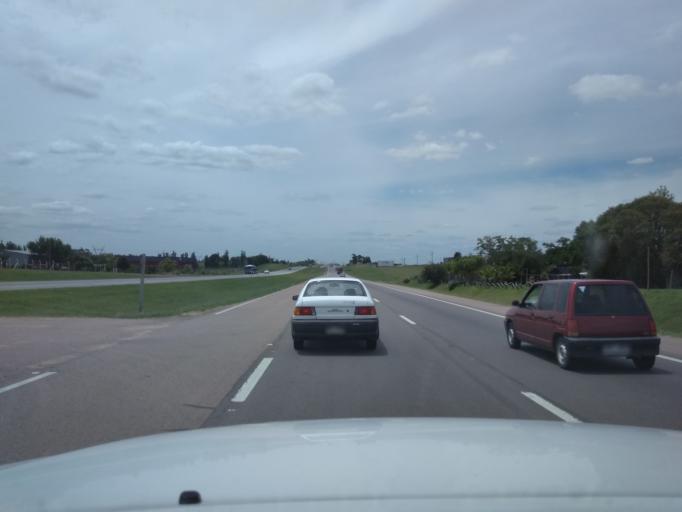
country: UY
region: Canelones
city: Las Piedras
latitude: -34.7375
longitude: -56.2504
